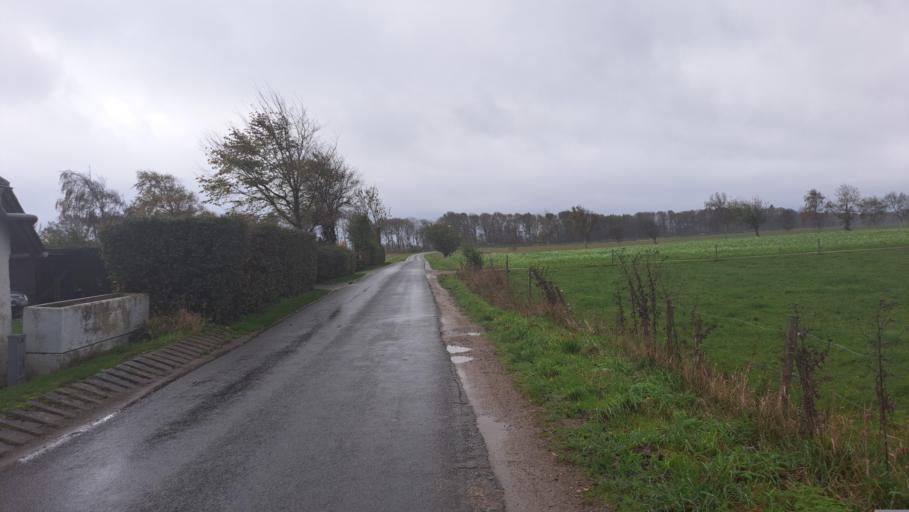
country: DK
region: Central Jutland
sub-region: Hedensted Kommune
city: Hedensted
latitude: 55.8297
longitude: 9.7315
